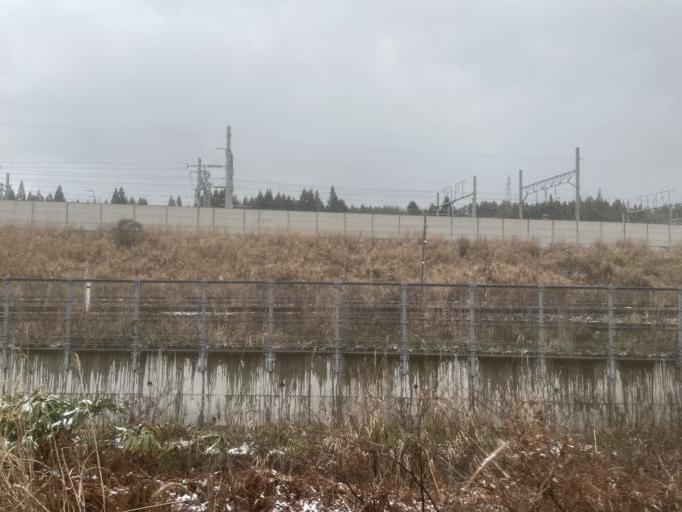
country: JP
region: Aomori
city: Goshogawara
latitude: 41.1430
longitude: 140.5165
